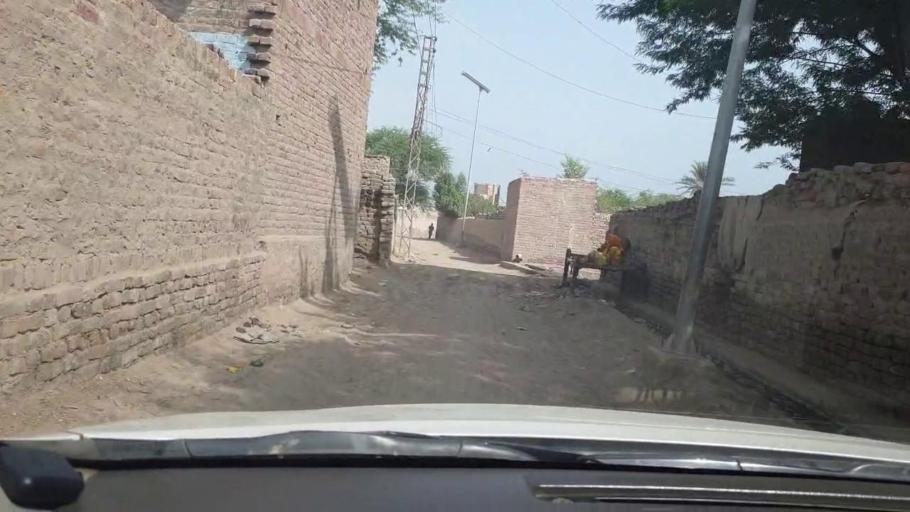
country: PK
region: Sindh
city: Shikarpur
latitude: 28.0072
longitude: 68.5927
